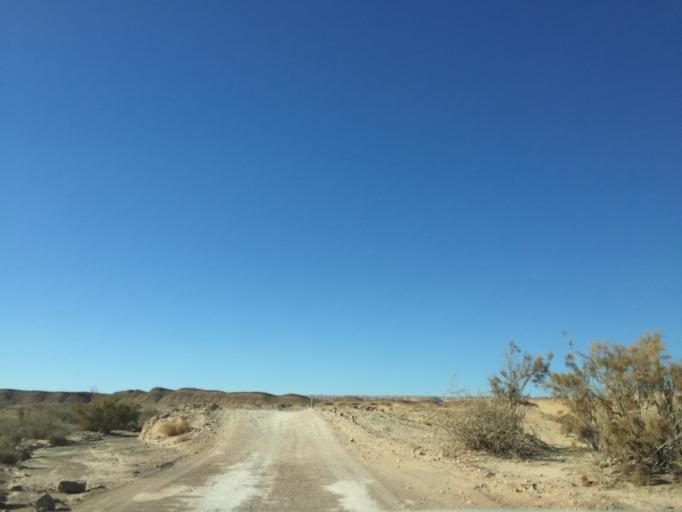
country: IL
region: Southern District
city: Mitzpe Ramon
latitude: 30.6135
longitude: 34.9088
